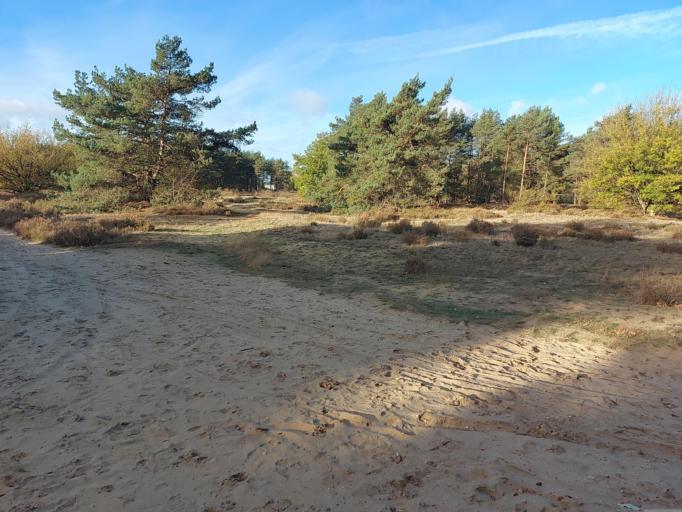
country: BE
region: Flanders
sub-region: Provincie Limburg
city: As
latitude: 51.0140
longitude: 5.5324
